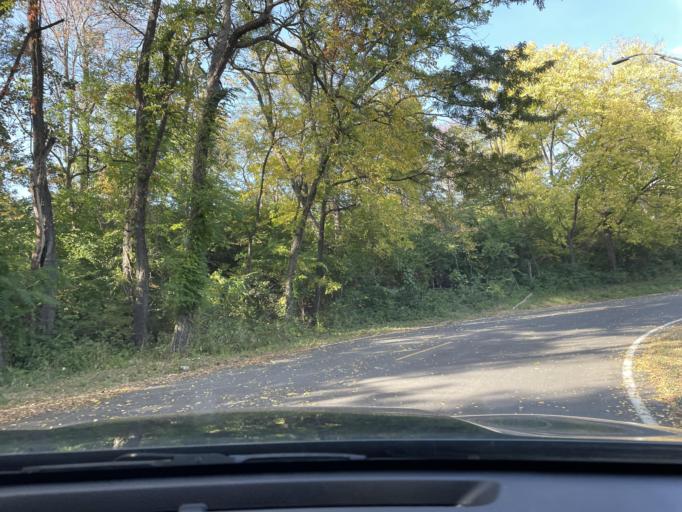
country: US
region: Kansas
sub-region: Doniphan County
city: Elwood
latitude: 39.7197
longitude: -94.8512
